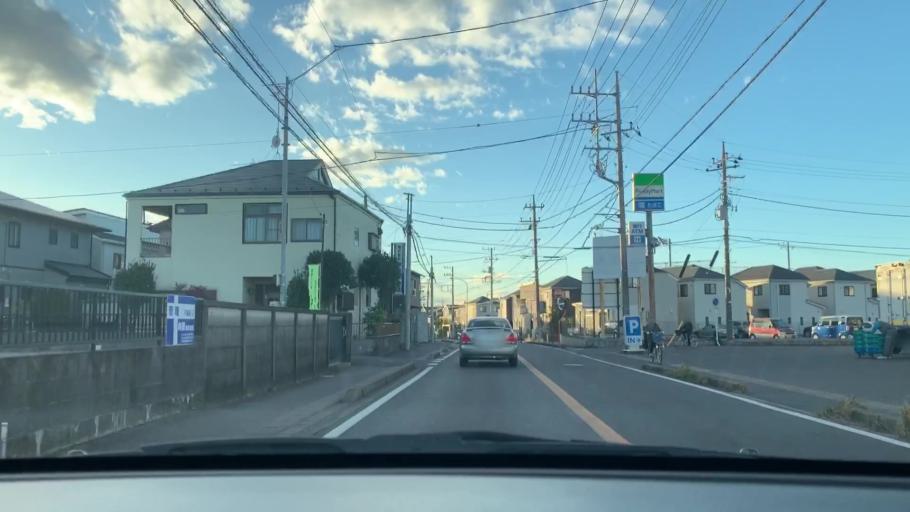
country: JP
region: Chiba
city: Nagareyama
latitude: 35.8871
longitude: 139.9241
